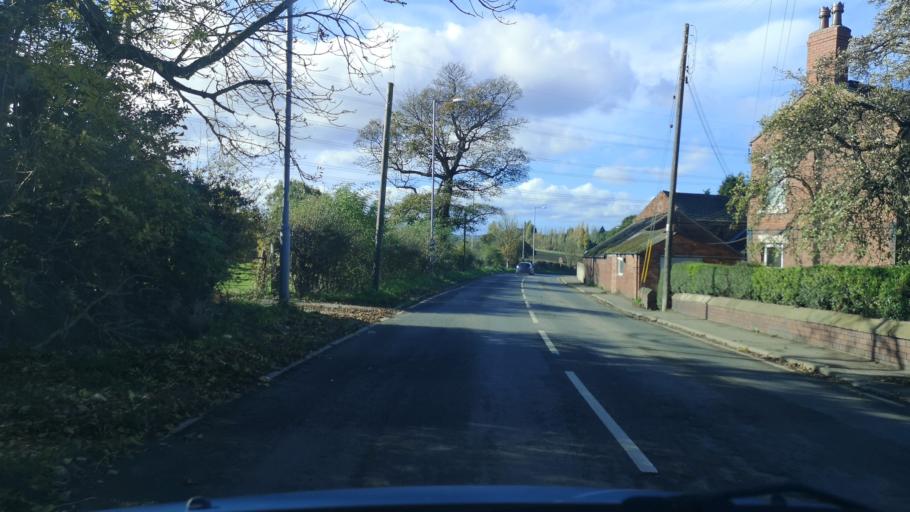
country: GB
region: England
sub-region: City and Borough of Wakefield
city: Normanton
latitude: 53.7055
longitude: -1.4429
